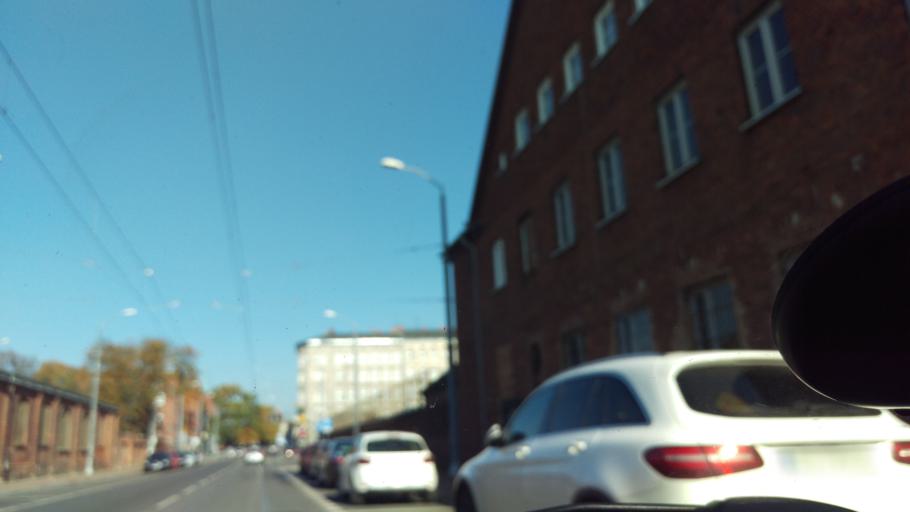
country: PL
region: West Pomeranian Voivodeship
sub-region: Szczecin
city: Szczecin
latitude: 53.4197
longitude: 14.5450
